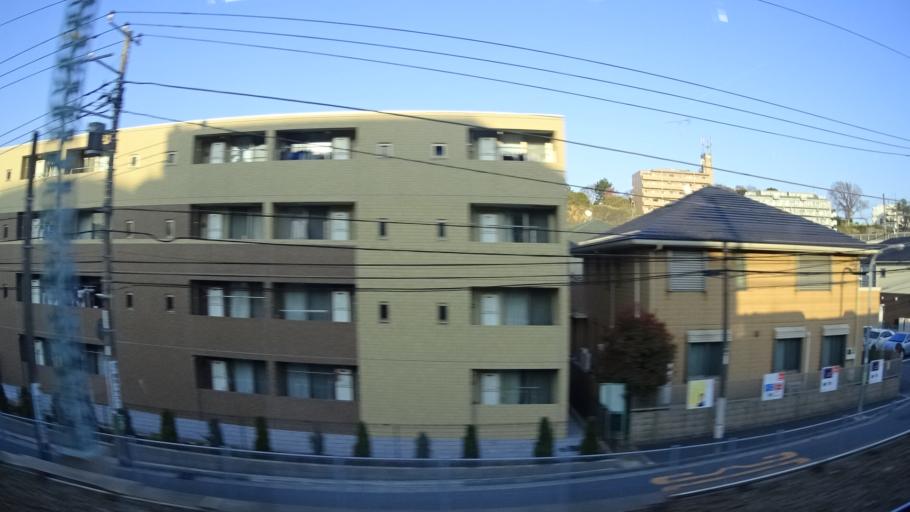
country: JP
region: Kanagawa
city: Yokohama
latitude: 35.3800
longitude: 139.6176
